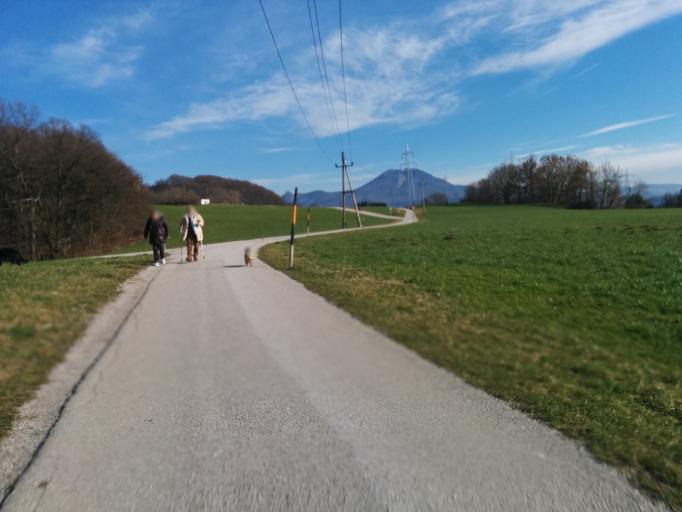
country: AT
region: Salzburg
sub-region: Politischer Bezirk Salzburg-Umgebung
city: Bergheim
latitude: 47.8396
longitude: 13.0272
